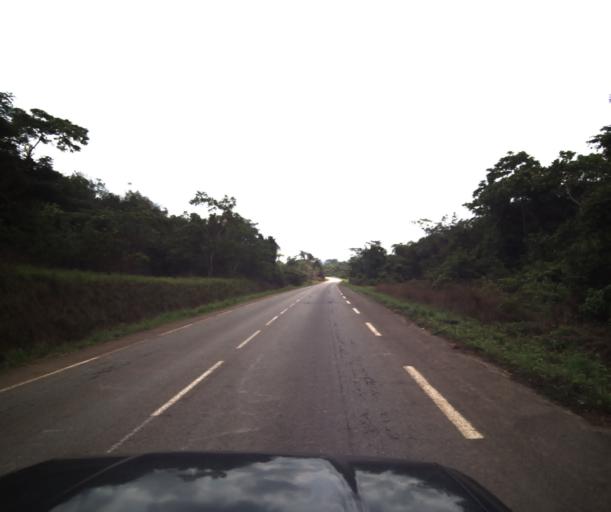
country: CM
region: Centre
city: Eseka
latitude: 3.8572
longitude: 10.5652
